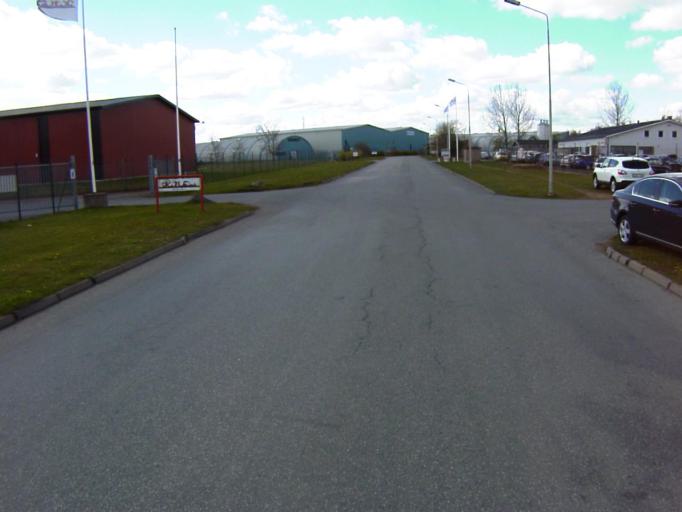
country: SE
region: Skane
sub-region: Kristianstads Kommun
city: Norra Asum
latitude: 56.0057
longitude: 14.1029
